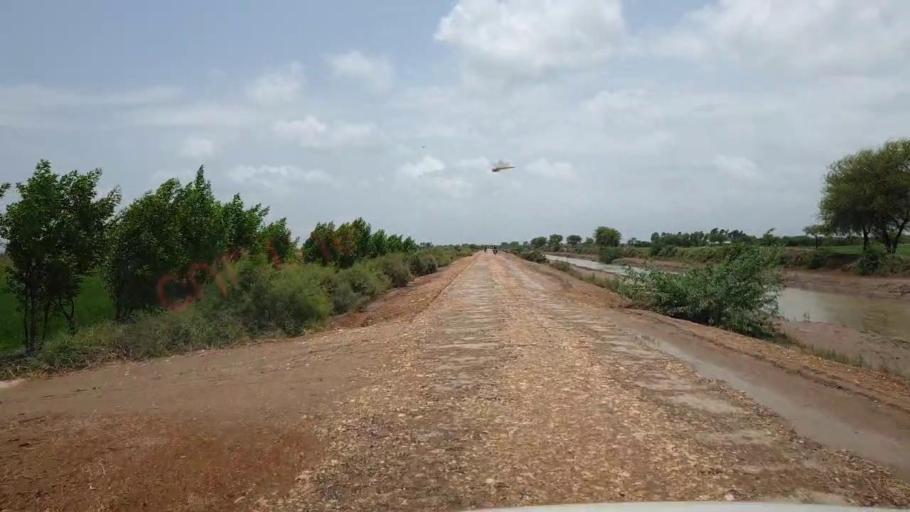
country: PK
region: Sindh
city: Kario
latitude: 24.7138
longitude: 68.5900
